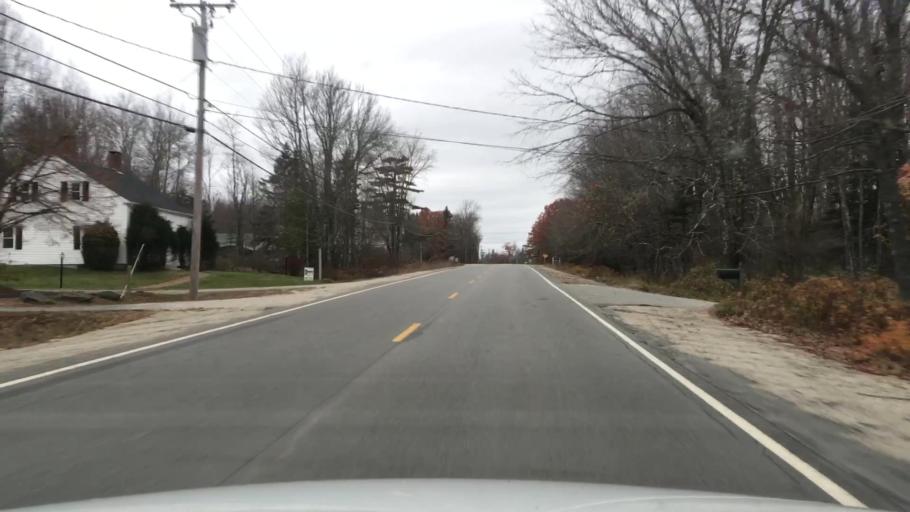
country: US
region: Maine
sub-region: Hancock County
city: Sedgwick
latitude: 44.3997
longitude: -68.5895
